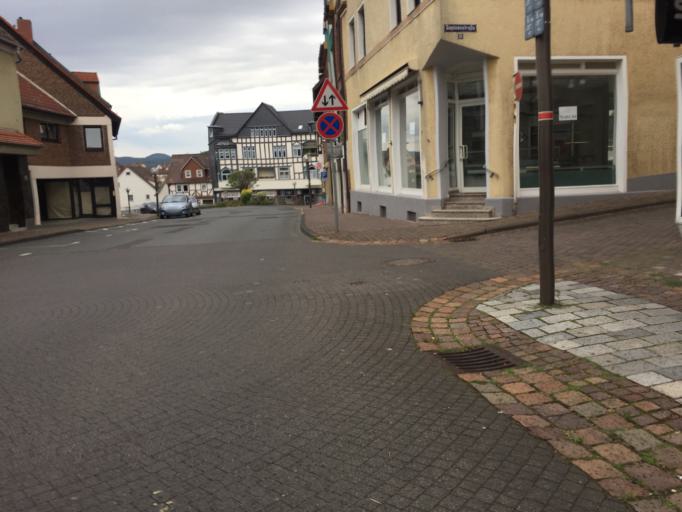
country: DE
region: Hesse
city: Bebra
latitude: 50.9707
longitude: 9.7923
